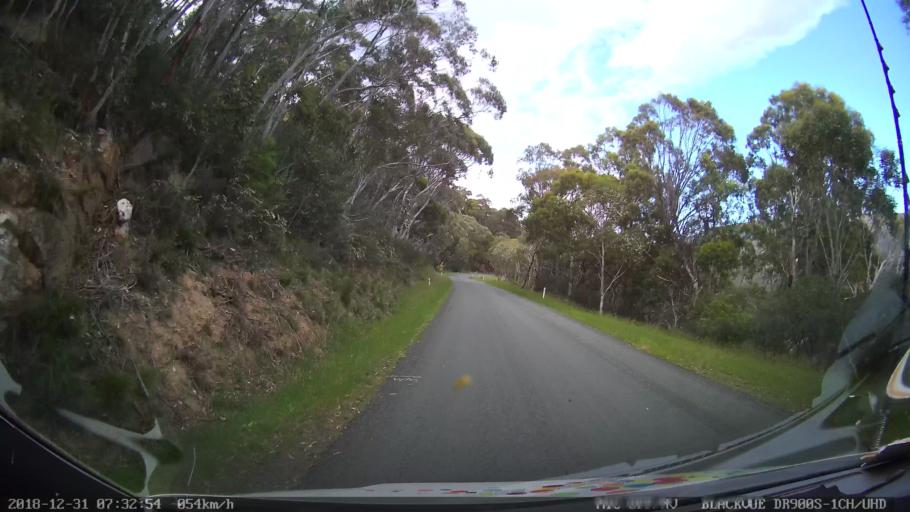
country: AU
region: New South Wales
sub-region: Snowy River
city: Jindabyne
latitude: -36.3305
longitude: 148.4613
